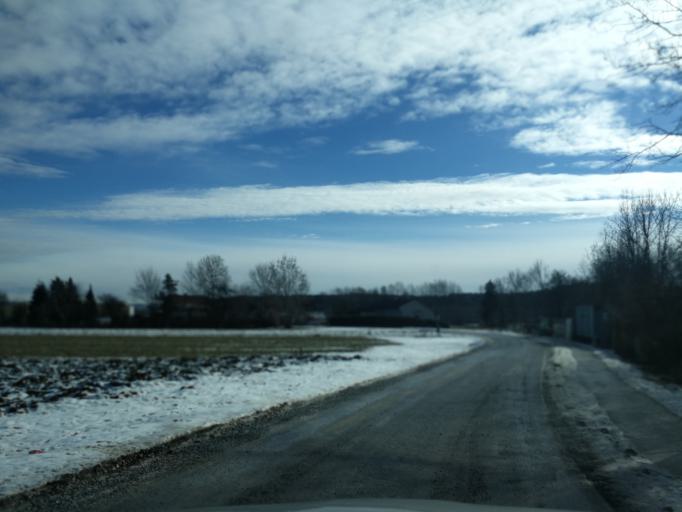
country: AT
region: Styria
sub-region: Politischer Bezirk Weiz
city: Ungerdorf
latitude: 47.1010
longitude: 15.6756
